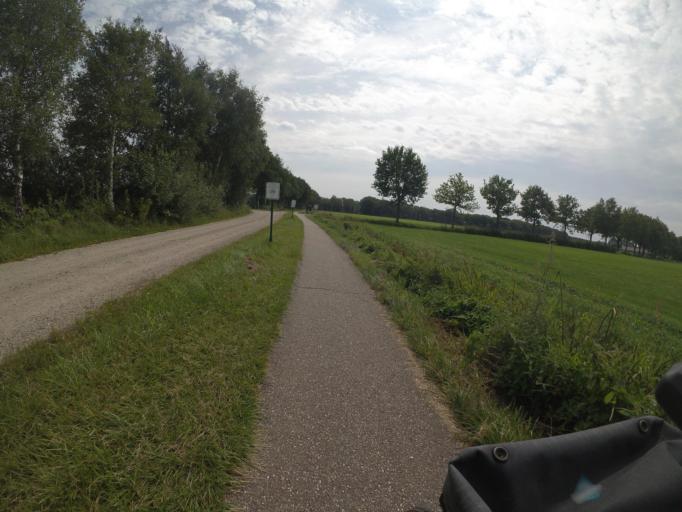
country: NL
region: North Brabant
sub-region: Bergeijk
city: Bergeyk
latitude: 51.3168
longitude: 5.3754
